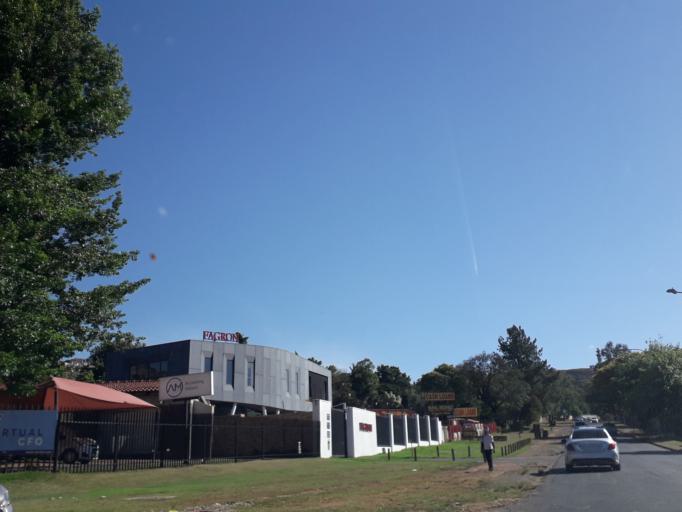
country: ZA
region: Gauteng
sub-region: City of Johannesburg Metropolitan Municipality
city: Roodepoort
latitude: -26.1460
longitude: 27.9525
